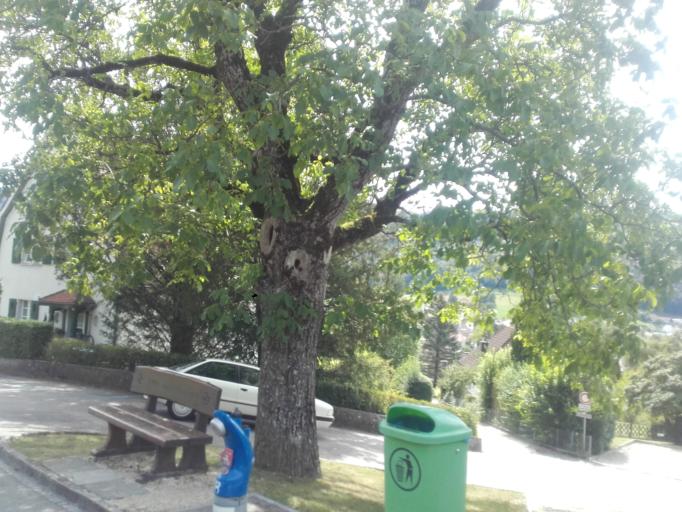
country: CH
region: Solothurn
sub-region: Bezirk Thal
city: Balsthal
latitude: 47.3188
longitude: 7.6912
